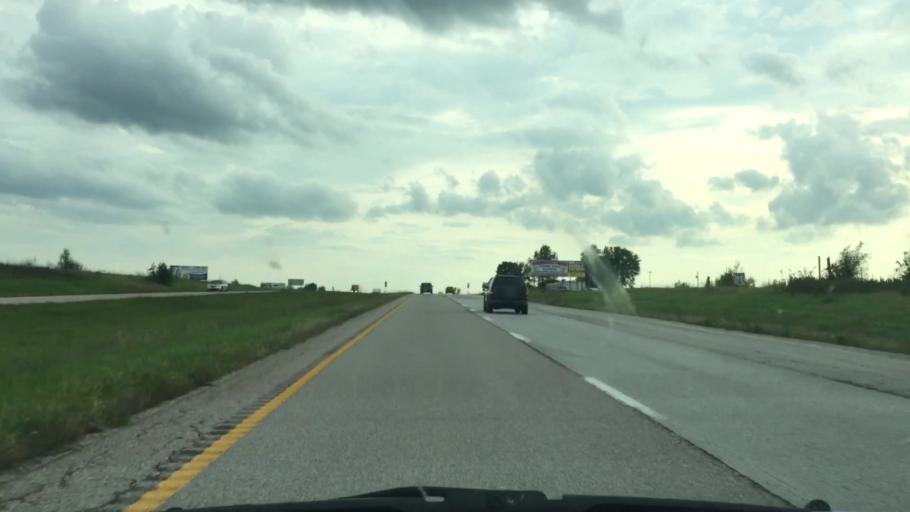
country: US
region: Missouri
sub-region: Clinton County
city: Lathrop
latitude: 39.5488
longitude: -94.2712
